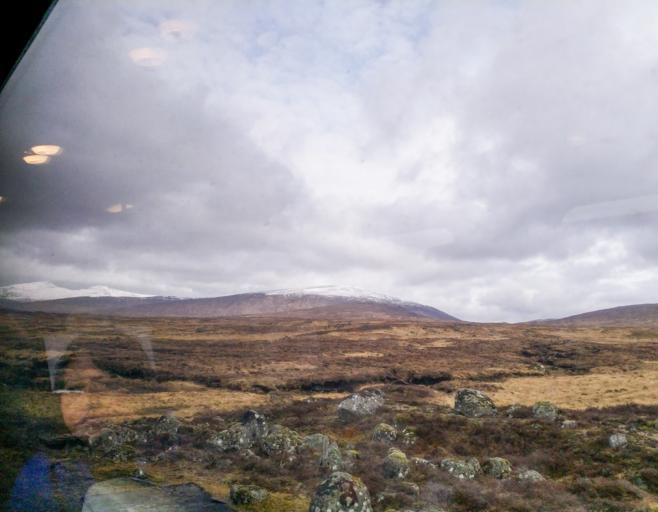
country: GB
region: Scotland
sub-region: Highland
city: Spean Bridge
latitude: 56.7285
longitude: -4.6427
